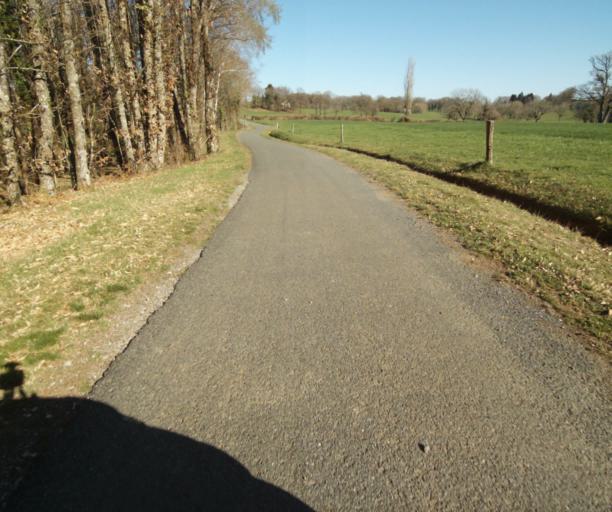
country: FR
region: Limousin
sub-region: Departement de la Correze
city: Chamboulive
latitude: 45.3966
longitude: 1.6749
